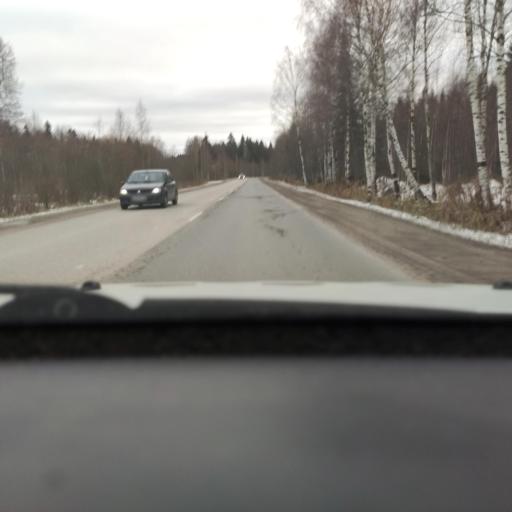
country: RU
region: Perm
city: Polazna
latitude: 58.1111
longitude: 56.4234
